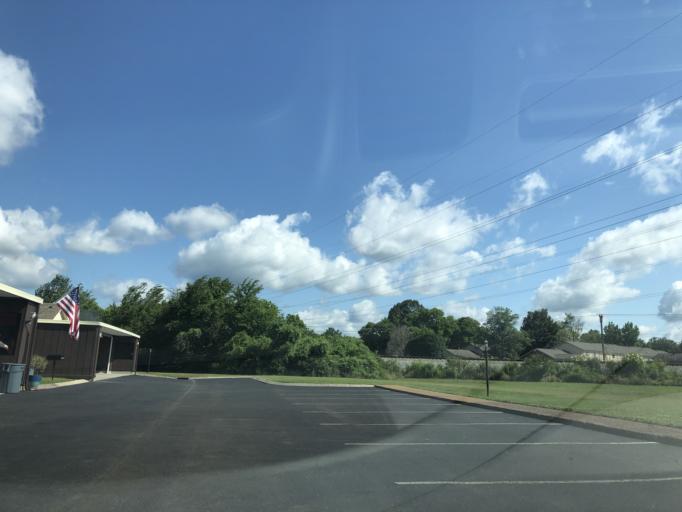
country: US
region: Tennessee
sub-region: Davidson County
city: Belle Meade
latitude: 36.0715
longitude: -86.9524
